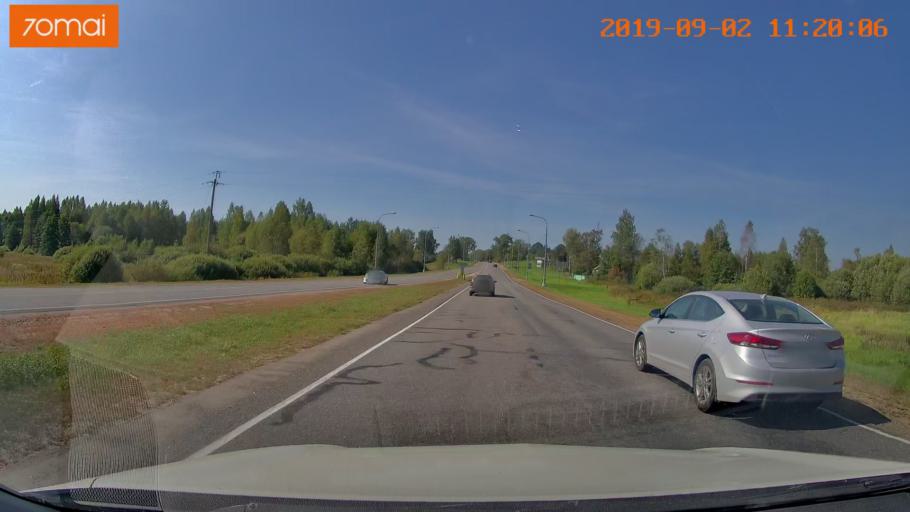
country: RU
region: Smolensk
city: Roslavl'
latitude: 54.0437
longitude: 33.0591
